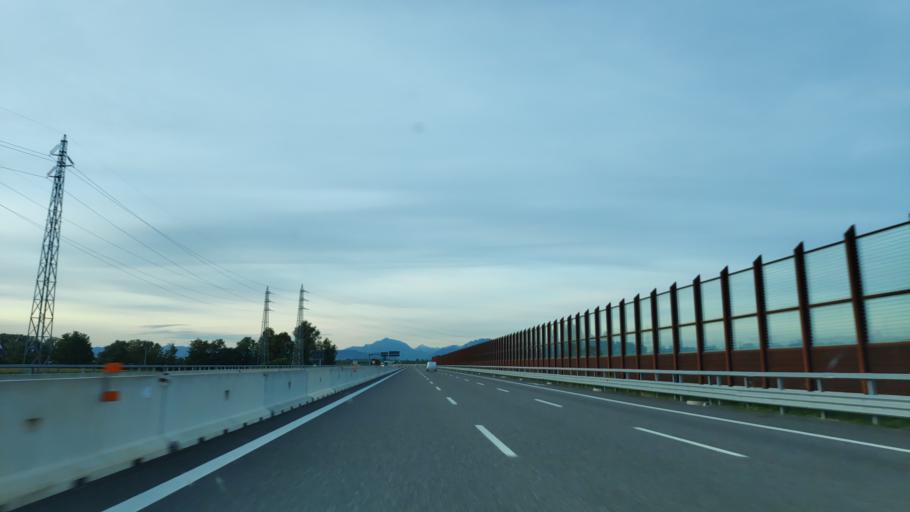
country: IT
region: Lombardy
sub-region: Citta metropolitana di Milano
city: Bellinzago Lombardo
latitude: 45.5250
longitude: 9.4400
